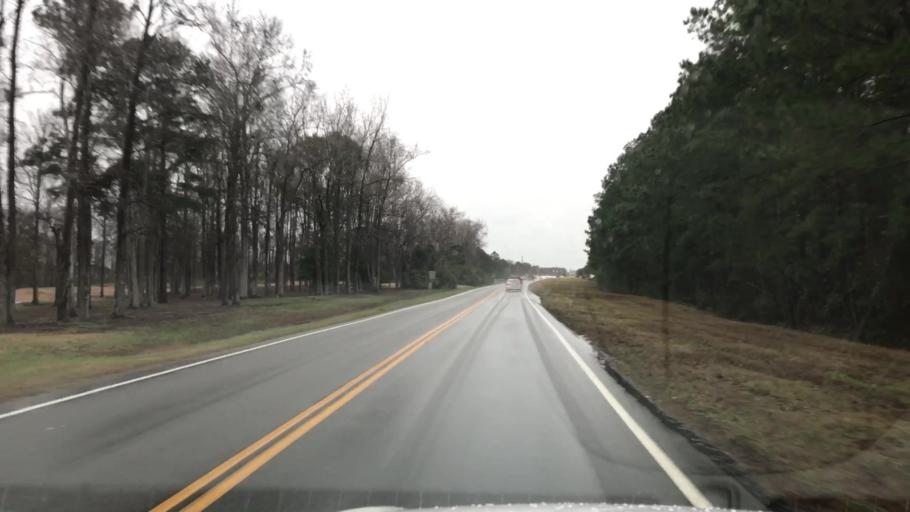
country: US
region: South Carolina
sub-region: Horry County
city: Myrtle Beach
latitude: 33.7331
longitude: -78.9042
